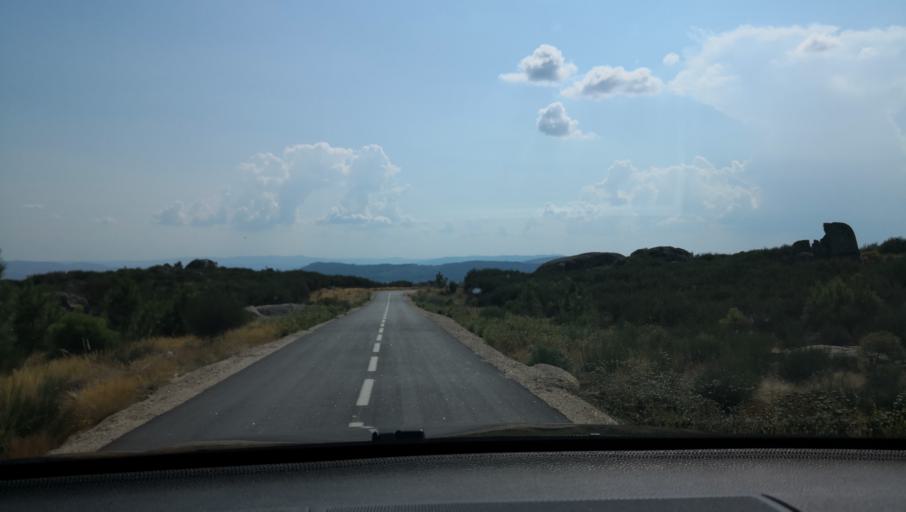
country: PT
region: Vila Real
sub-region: Sabrosa
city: Sabrosa
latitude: 41.2858
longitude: -7.6135
